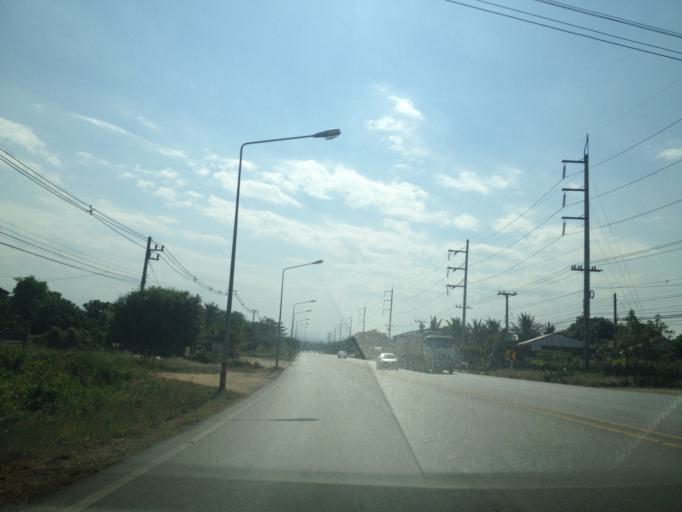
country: TH
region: Chiang Mai
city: Chom Thong
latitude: 18.3529
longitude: 98.6793
